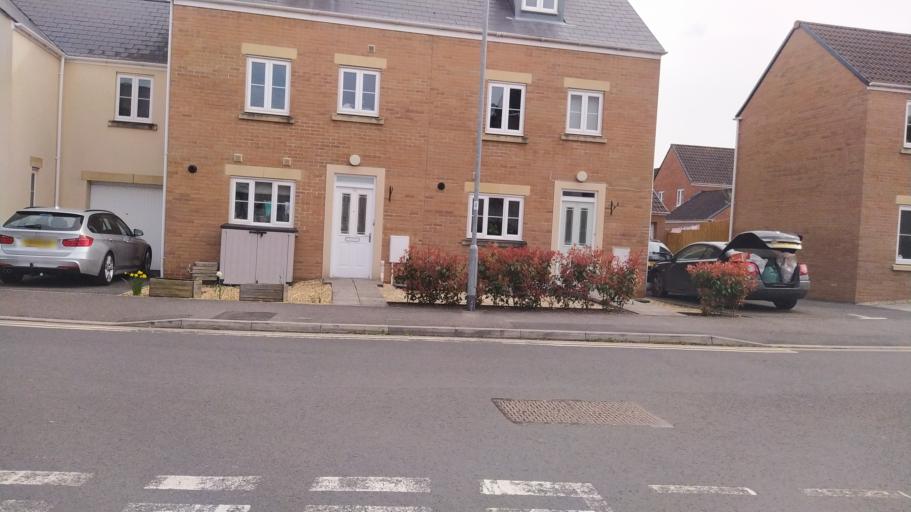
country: GB
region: England
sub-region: Somerset
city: Taunton
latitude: 51.0258
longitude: -3.1482
